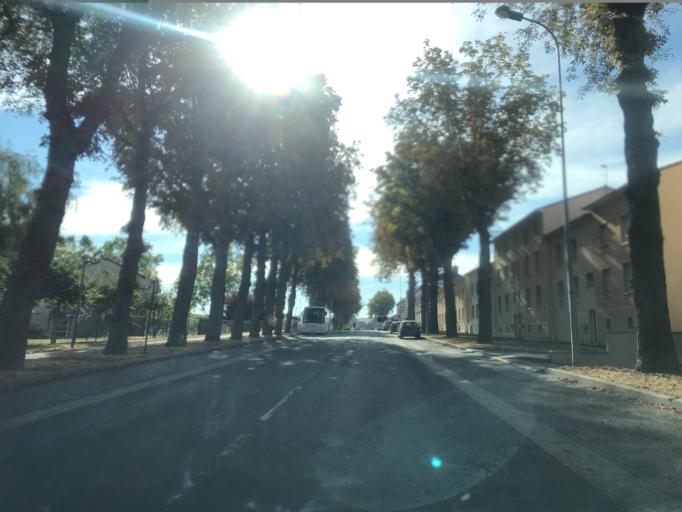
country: FR
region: Champagne-Ardenne
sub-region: Departement de la Marne
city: Pierry
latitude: 49.0296
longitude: 3.9542
